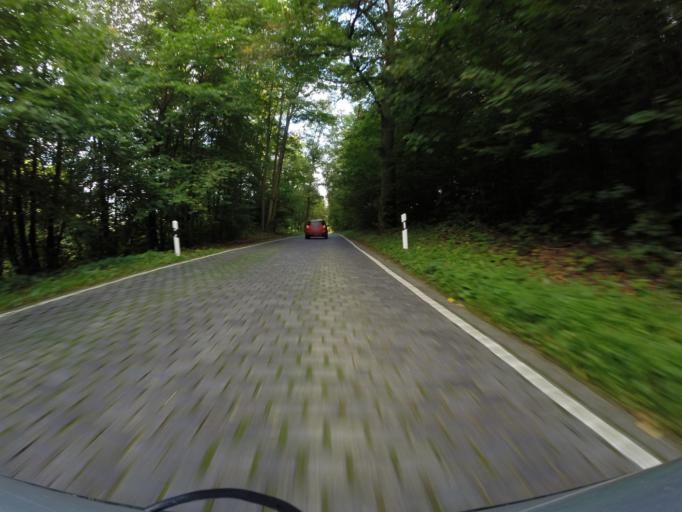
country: DE
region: Thuringia
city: Jena
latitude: 50.9567
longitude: 11.5942
